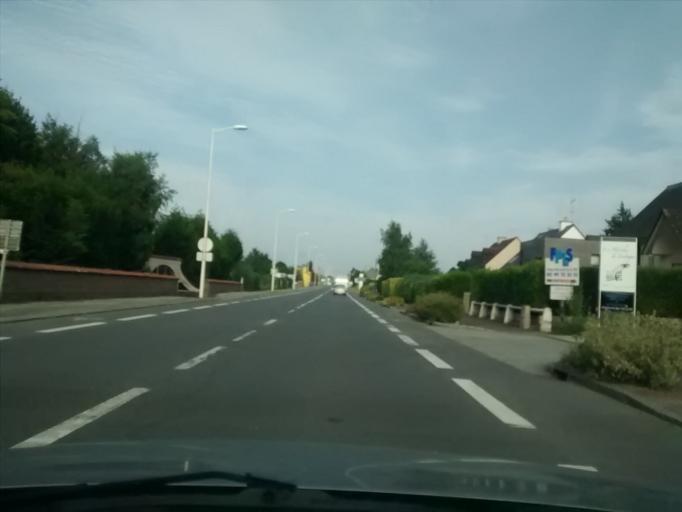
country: FR
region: Brittany
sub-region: Departement d'Ille-et-Vilaine
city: Vitre
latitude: 48.1216
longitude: -1.1836
